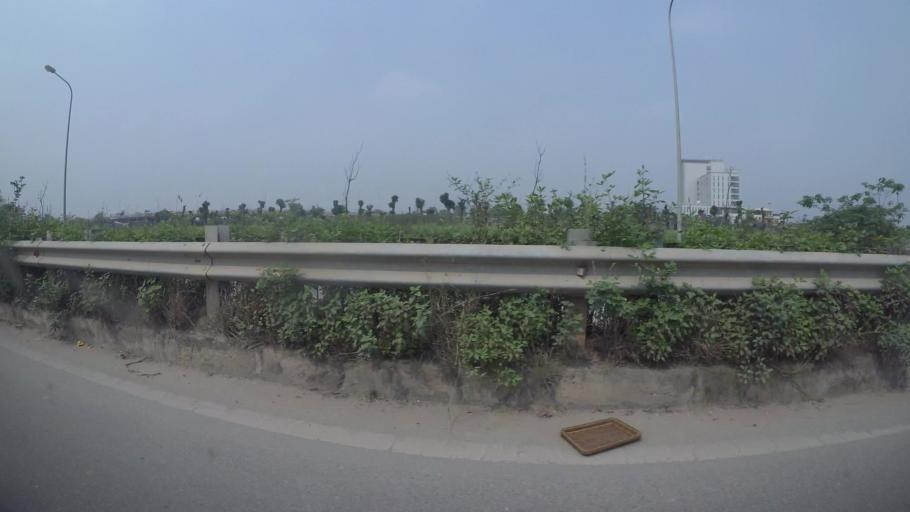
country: VN
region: Ha Noi
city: Cau Dien
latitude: 21.0115
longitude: 105.7488
